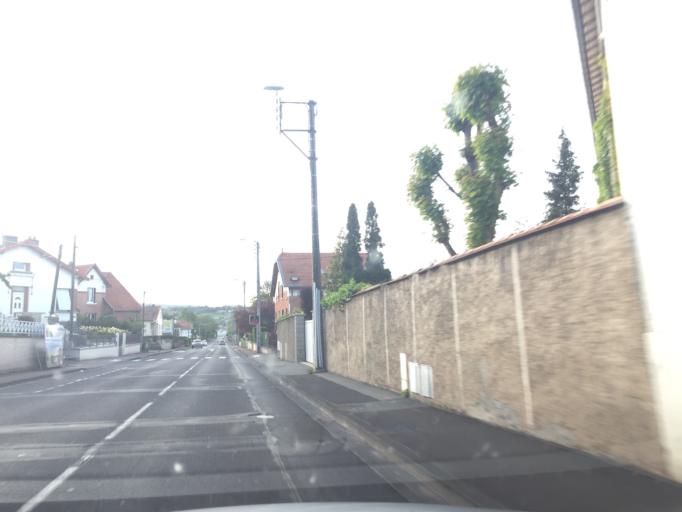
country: FR
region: Auvergne
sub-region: Departement du Puy-de-Dome
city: Riom
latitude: 45.8963
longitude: 3.1079
